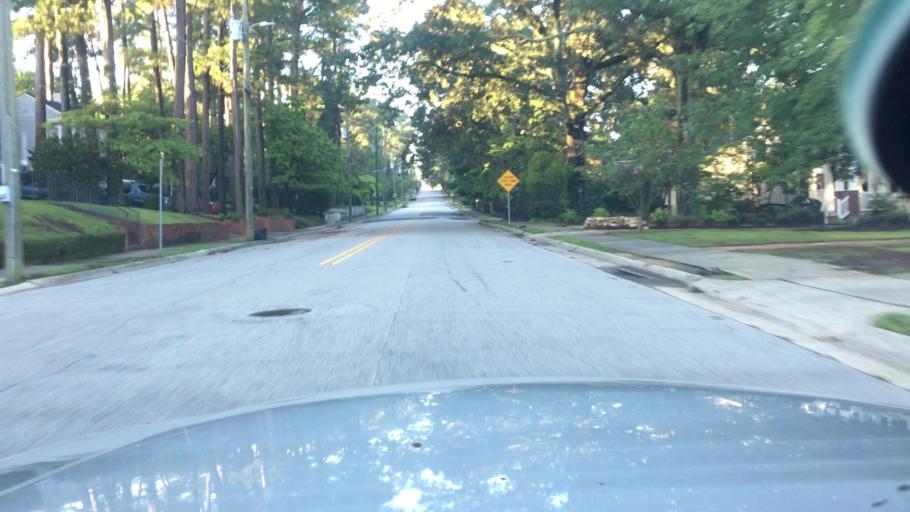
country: US
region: North Carolina
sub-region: Cumberland County
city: Fayetteville
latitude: 35.0654
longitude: -78.9050
